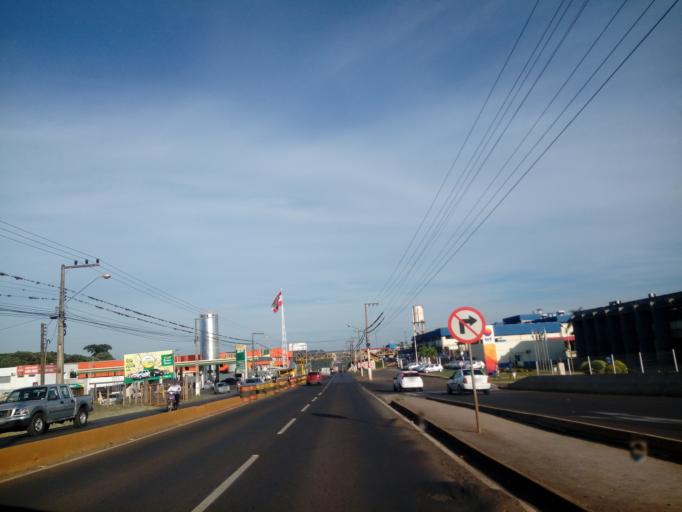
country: BR
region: Santa Catarina
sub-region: Chapeco
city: Chapeco
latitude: -27.0981
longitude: -52.6492
